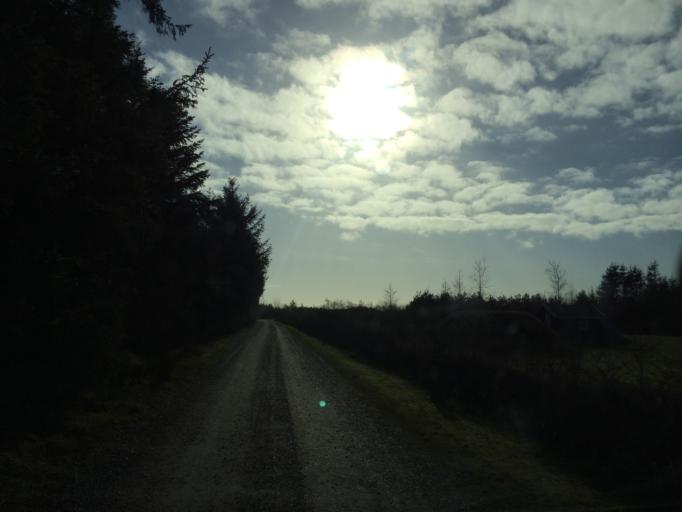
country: DK
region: Central Jutland
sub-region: Holstebro Kommune
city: Ulfborg
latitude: 56.2693
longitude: 8.3315
